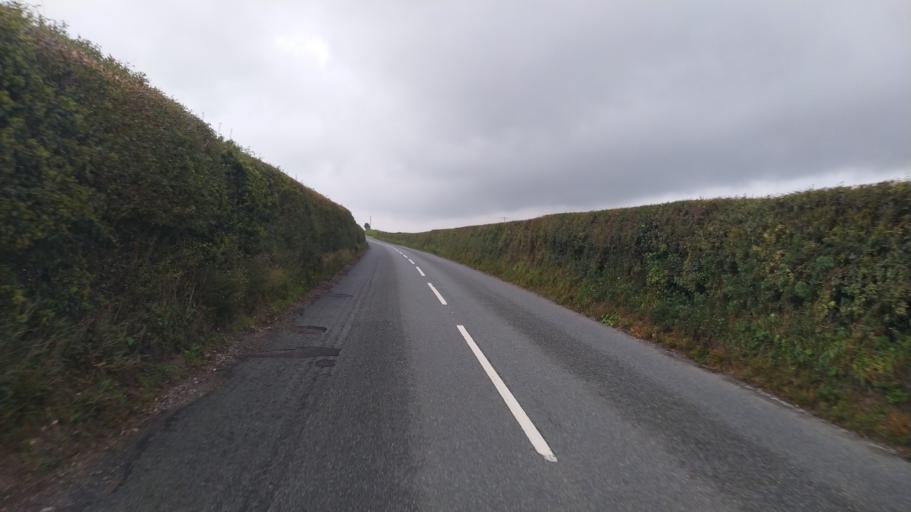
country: GB
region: England
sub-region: Wiltshire
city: Salisbury
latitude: 51.1096
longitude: -1.7670
